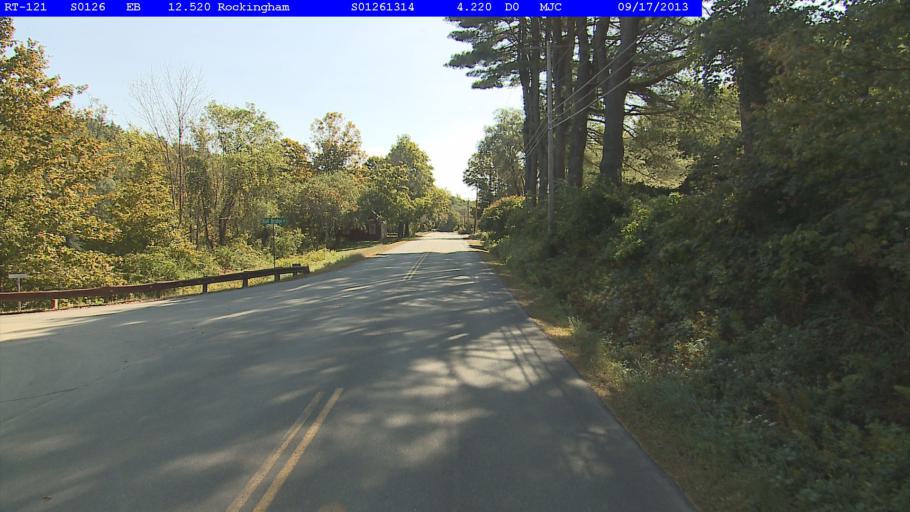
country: US
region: Vermont
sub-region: Windham County
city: Bellows Falls
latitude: 43.1372
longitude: -72.4877
